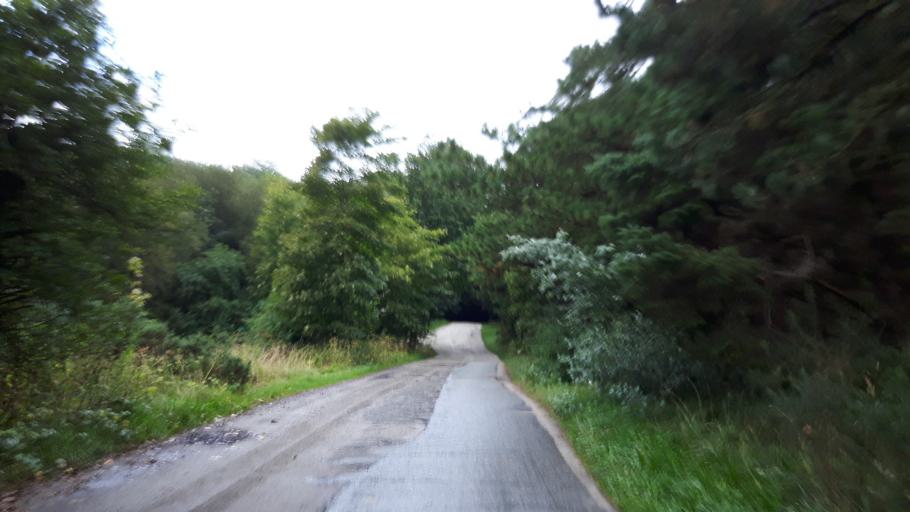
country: NL
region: Friesland
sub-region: Gemeente Ameland
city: Nes
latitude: 53.4526
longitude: 5.7568
